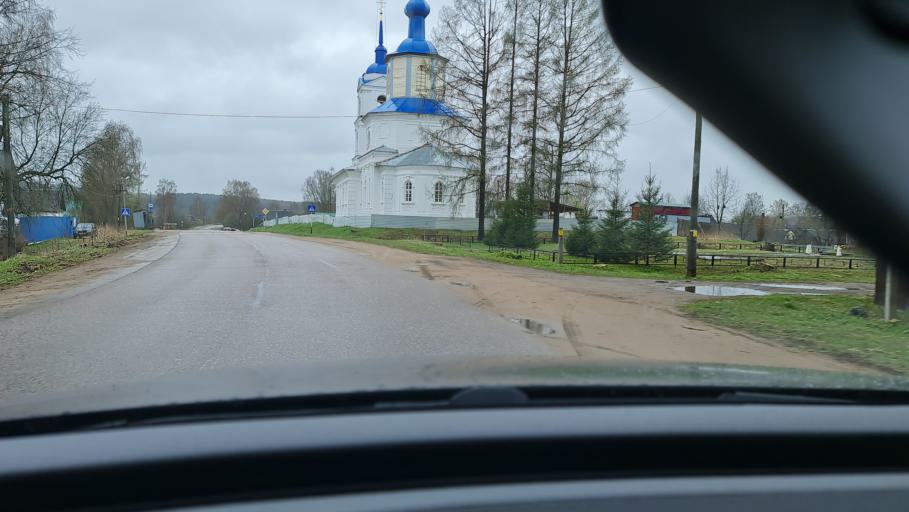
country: RU
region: Novgorod
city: Valday
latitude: 58.0370
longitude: 32.9567
